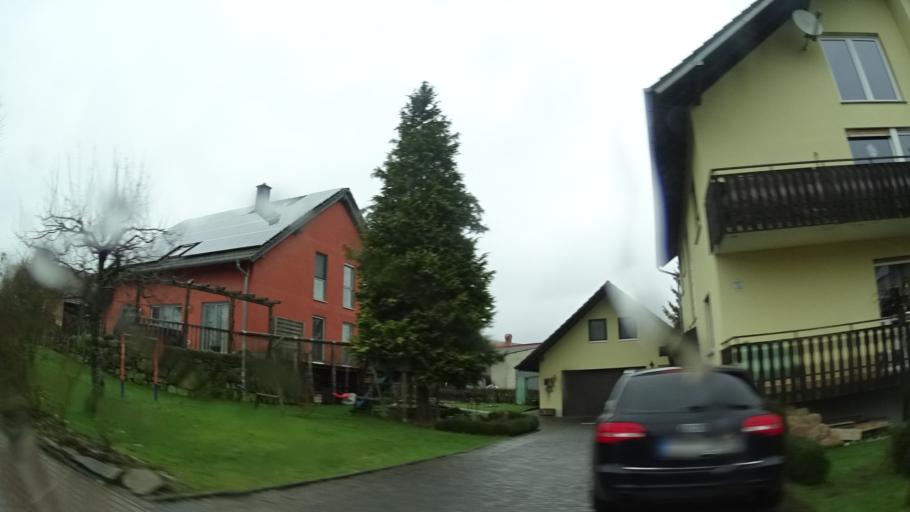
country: DE
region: Hesse
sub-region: Regierungsbezirk Kassel
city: Dipperz
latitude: 50.5605
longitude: 9.7919
